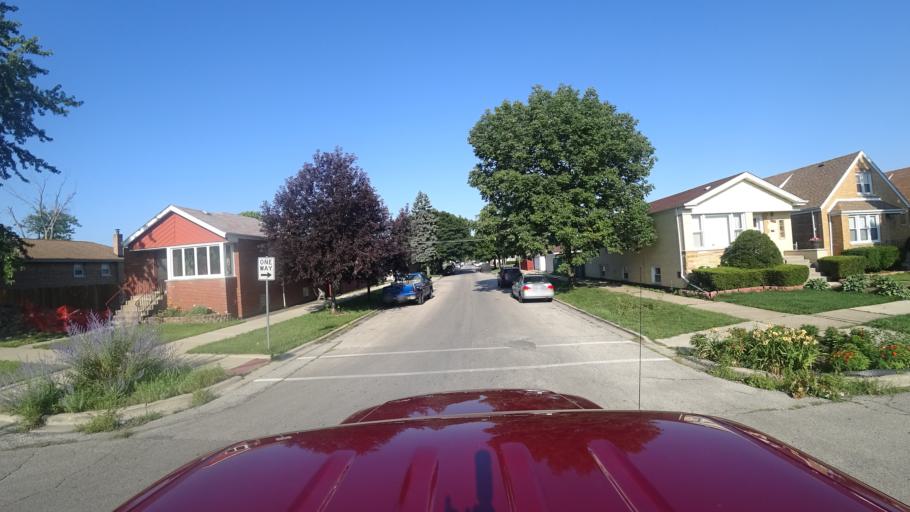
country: US
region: Illinois
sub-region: Cook County
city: Cicero
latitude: 41.7951
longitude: -87.7195
